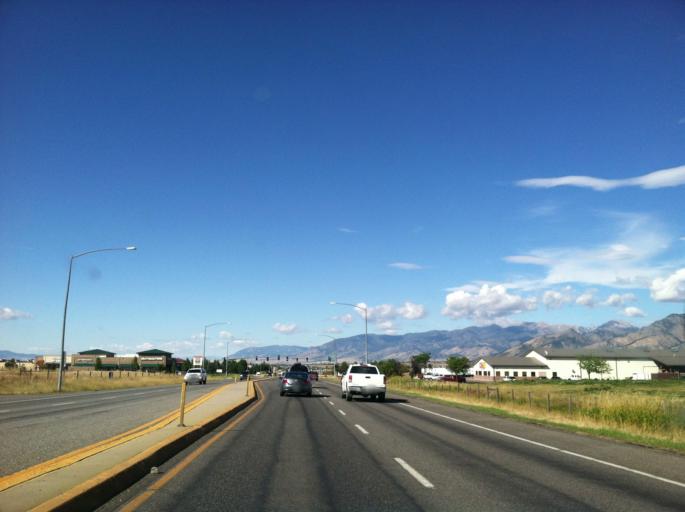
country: US
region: Montana
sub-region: Gallatin County
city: Bozeman
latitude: 45.7052
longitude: -111.0651
